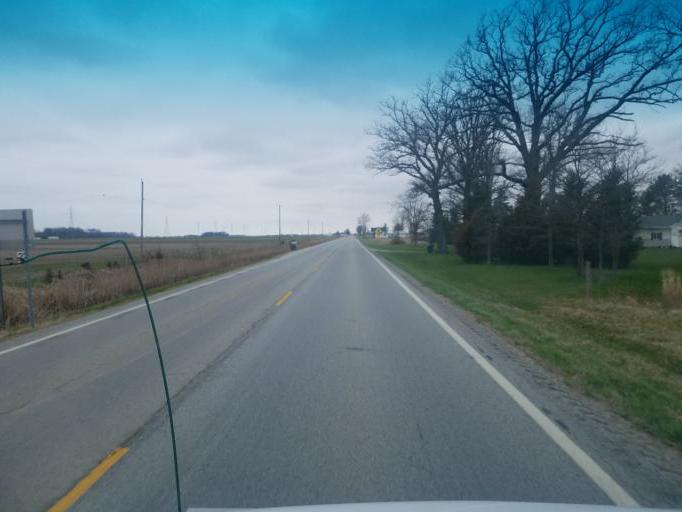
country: US
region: Ohio
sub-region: Van Wert County
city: Van Wert
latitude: 40.9321
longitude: -84.4697
